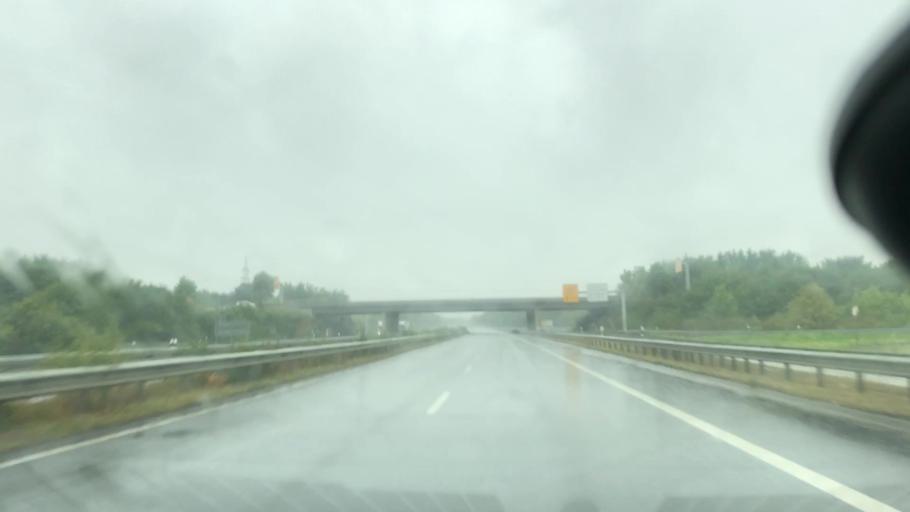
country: DE
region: North Rhine-Westphalia
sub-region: Regierungsbezirk Detmold
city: Minden
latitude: 52.2650
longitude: 8.9133
